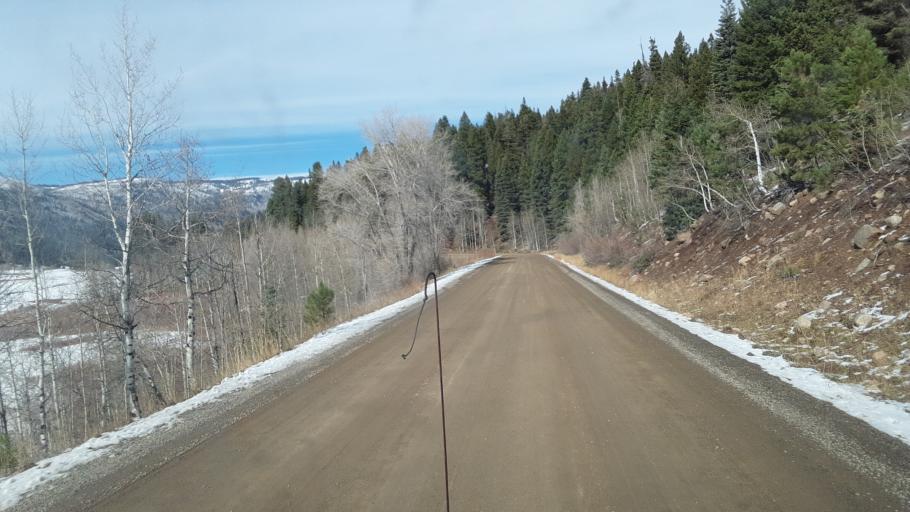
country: US
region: Colorado
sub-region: La Plata County
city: Bayfield
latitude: 37.4095
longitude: -107.6619
